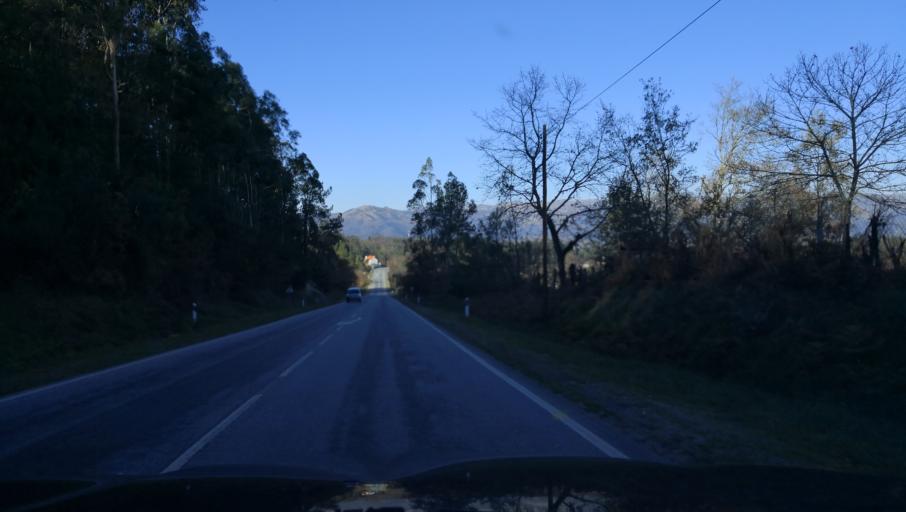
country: PT
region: Viseu
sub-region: Vouzela
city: Vouzela
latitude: 40.7011
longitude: -8.1405
